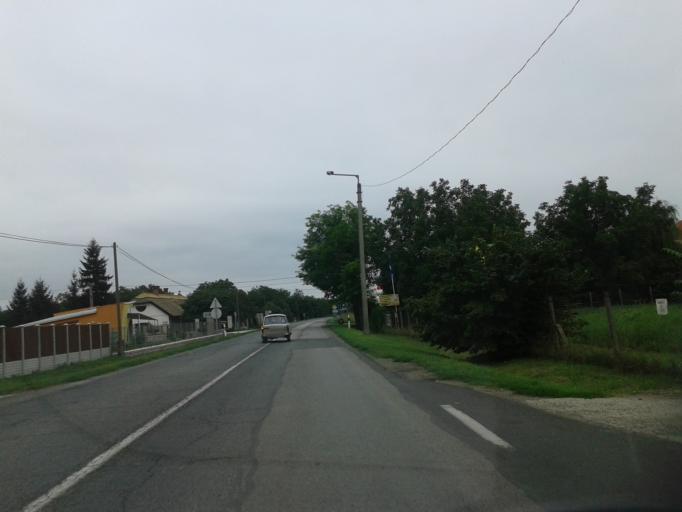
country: HU
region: Bacs-Kiskun
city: Tass
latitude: 47.0252
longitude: 19.0220
